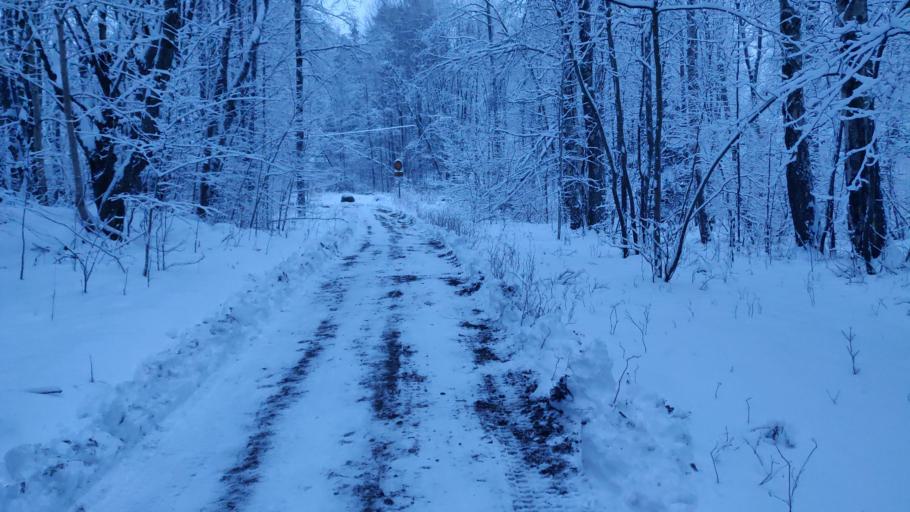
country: SE
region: Vaestra Goetaland
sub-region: Uddevalla Kommun
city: Uddevalla
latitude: 58.3394
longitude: 11.9427
